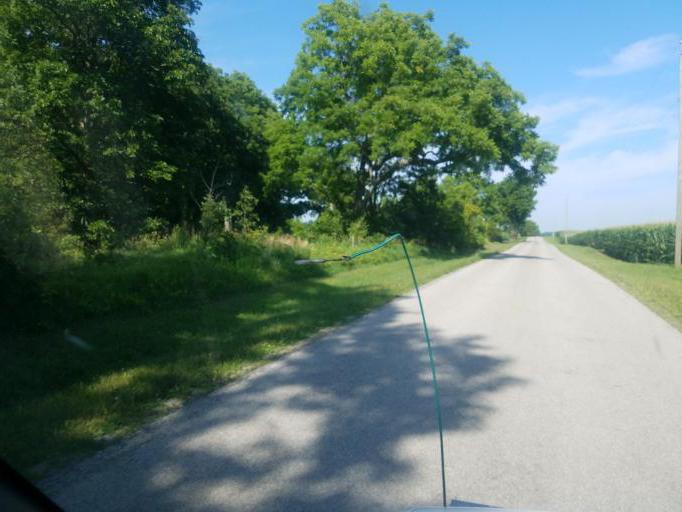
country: US
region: Ohio
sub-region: Hardin County
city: Kenton
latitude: 40.5532
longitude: -83.6615
